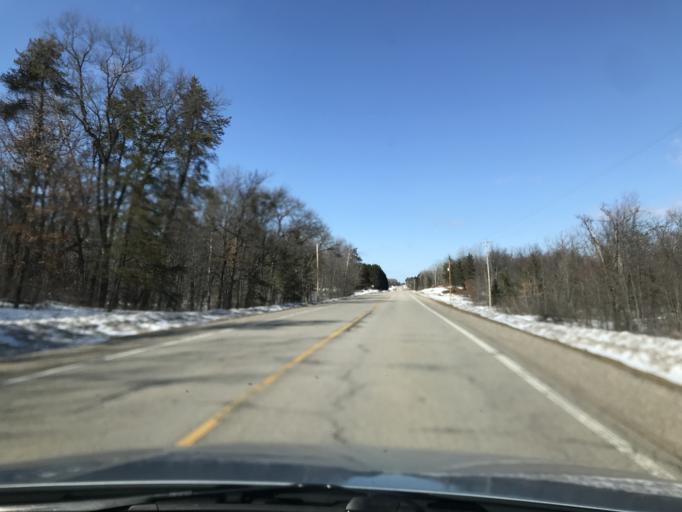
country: US
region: Wisconsin
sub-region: Marinette County
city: Niagara
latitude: 45.3420
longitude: -88.1015
